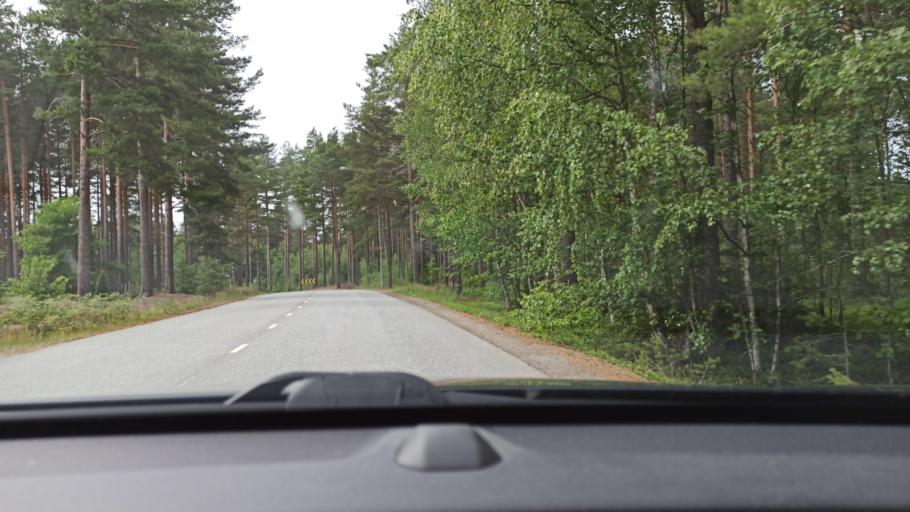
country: FI
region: Satakunta
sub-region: Pori
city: Luvia
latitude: 61.5747
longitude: 21.5255
